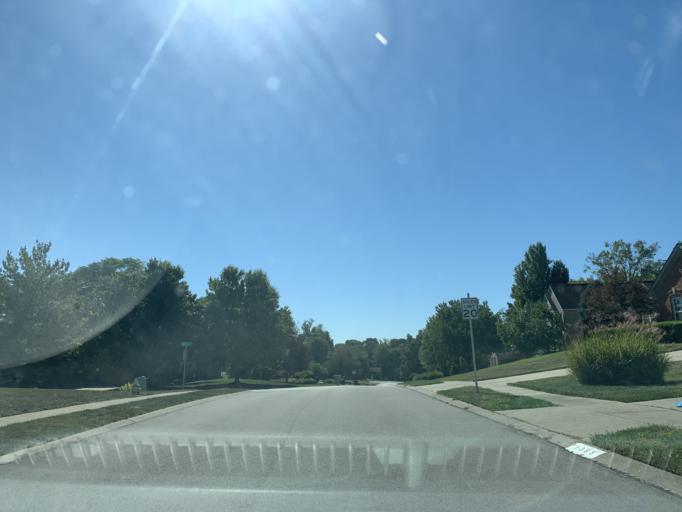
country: US
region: Kentucky
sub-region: Boone County
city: Francisville
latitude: 39.1007
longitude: -84.7300
